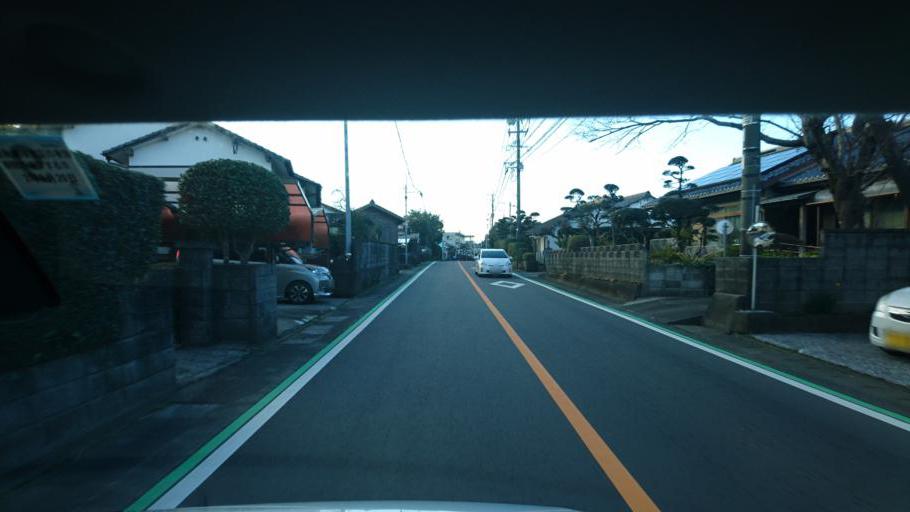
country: JP
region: Miyazaki
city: Miyazaki-shi
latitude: 31.8340
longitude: 131.4333
